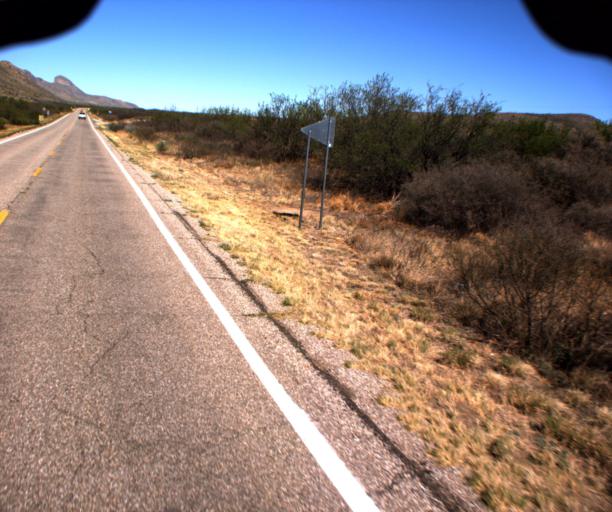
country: US
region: Arizona
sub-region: Cochise County
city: Huachuca City
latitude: 31.6934
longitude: -110.4093
